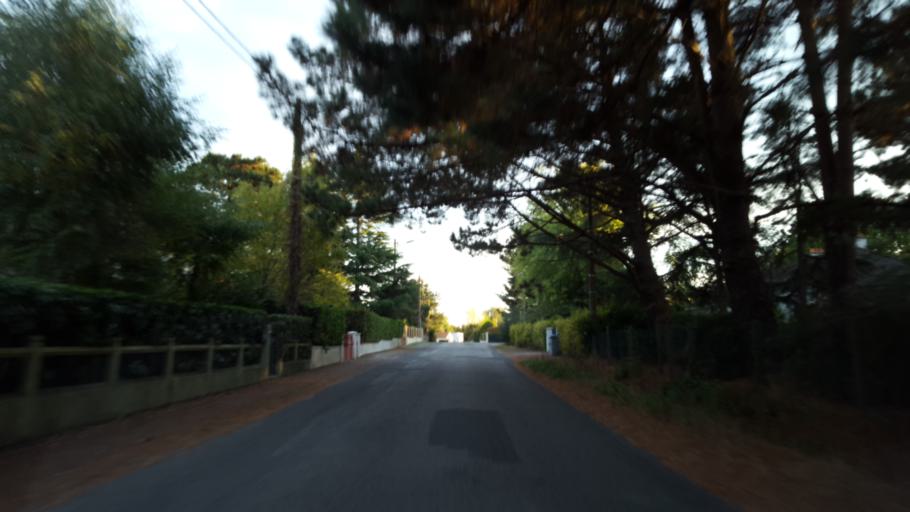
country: FR
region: Pays de la Loire
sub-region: Departement de la Loire-Atlantique
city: Basse-Goulaine
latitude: 47.2106
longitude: -1.4752
